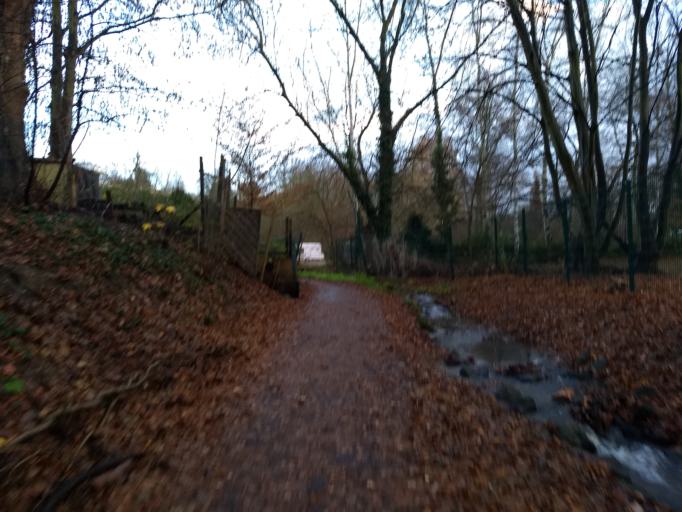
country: DE
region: North Rhine-Westphalia
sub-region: Regierungsbezirk Koln
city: Bonn
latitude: 50.7170
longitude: 7.0878
